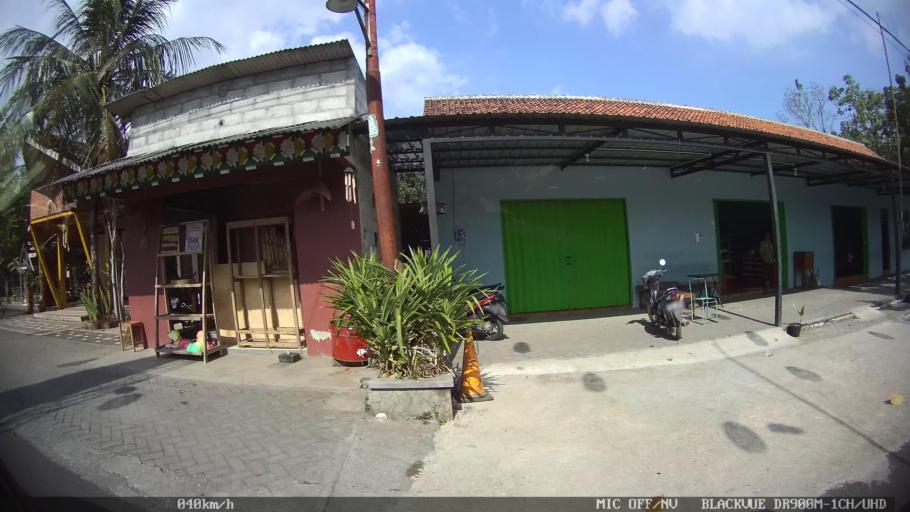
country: ID
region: Daerah Istimewa Yogyakarta
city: Kasihan
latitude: -7.8551
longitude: 110.3015
